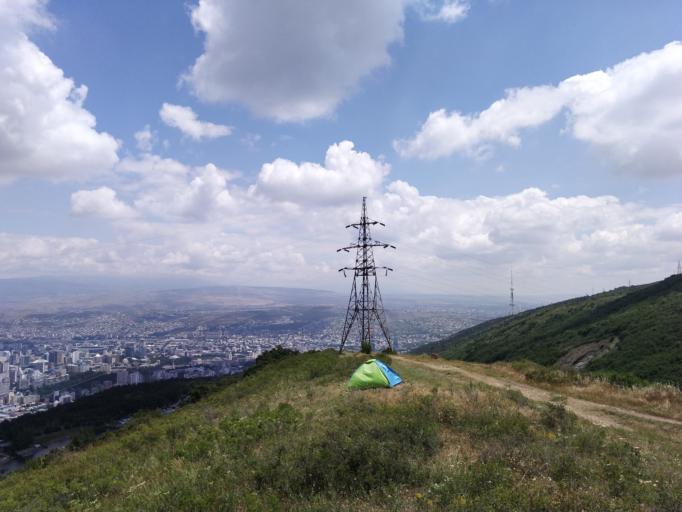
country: GE
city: Tsqnet'i
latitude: 41.6970
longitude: 44.7493
